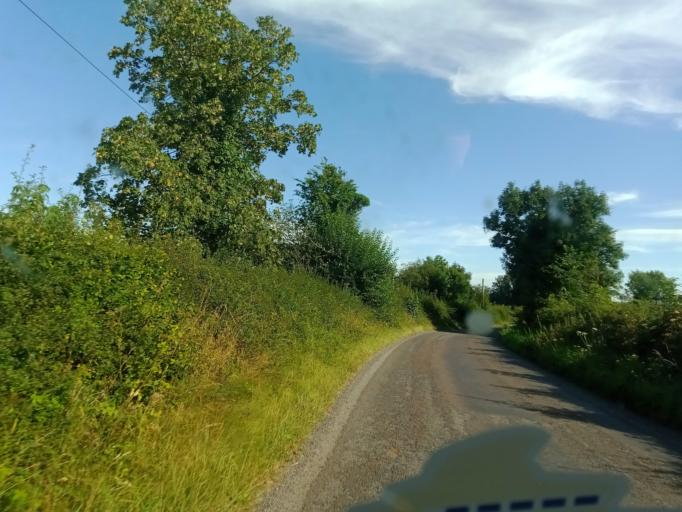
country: IE
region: Leinster
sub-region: Kilkenny
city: Ballyragget
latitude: 52.7657
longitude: -7.3909
